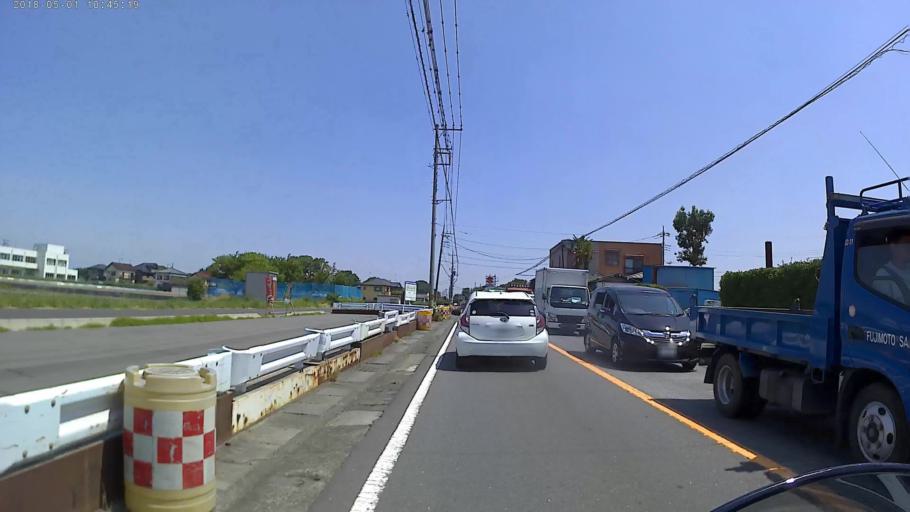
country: JP
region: Kanagawa
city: Minami-rinkan
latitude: 35.4511
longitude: 139.4703
